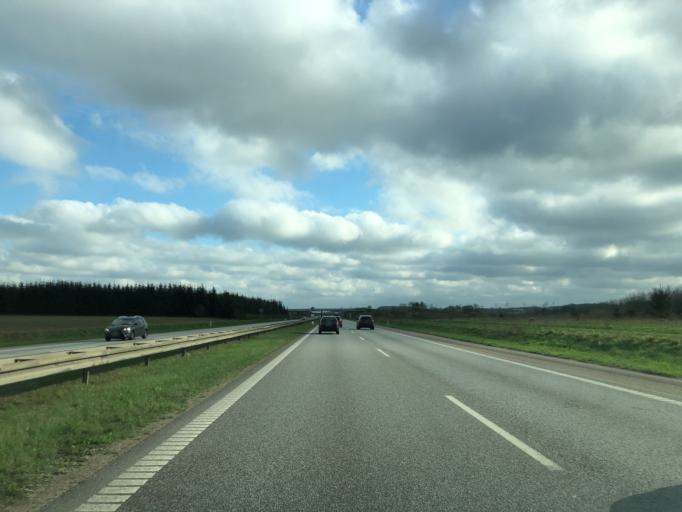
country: DK
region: North Denmark
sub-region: Alborg Kommune
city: Svenstrup
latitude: 56.9762
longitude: 9.8785
